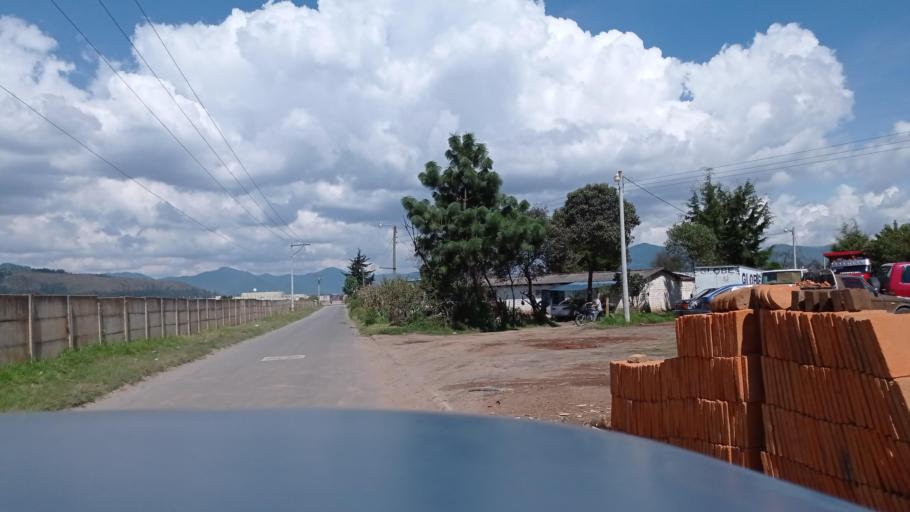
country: GT
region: Quetzaltenango
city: Olintepeque
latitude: 14.8691
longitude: -91.4951
